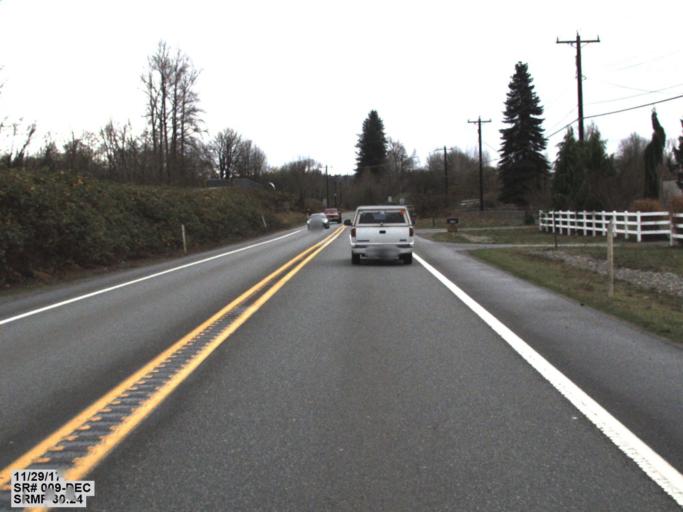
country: US
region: Washington
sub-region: Snohomish County
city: Arlington
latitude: 48.2086
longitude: -122.1311
